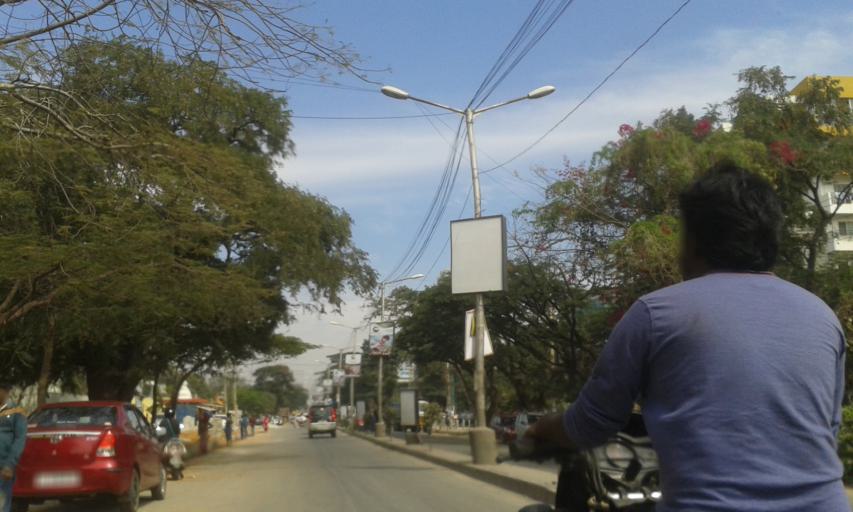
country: IN
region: Karnataka
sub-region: Bangalore Rural
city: Hoskote
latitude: 12.9712
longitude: 77.7501
